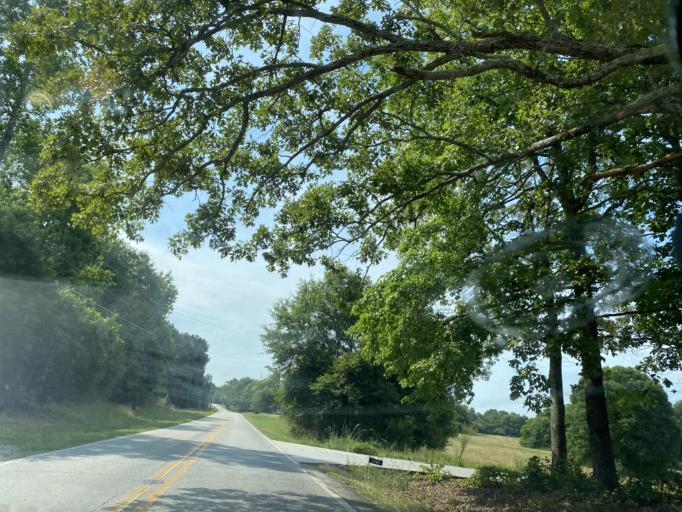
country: US
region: Georgia
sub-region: Coweta County
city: Grantville
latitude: 33.1938
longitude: -84.7151
